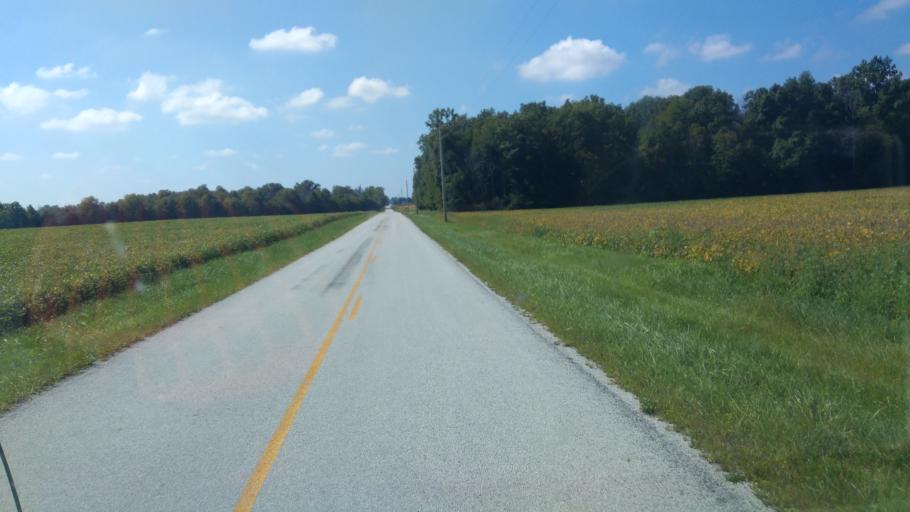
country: US
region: Ohio
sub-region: Hardin County
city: Ada
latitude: 40.7473
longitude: -83.7161
